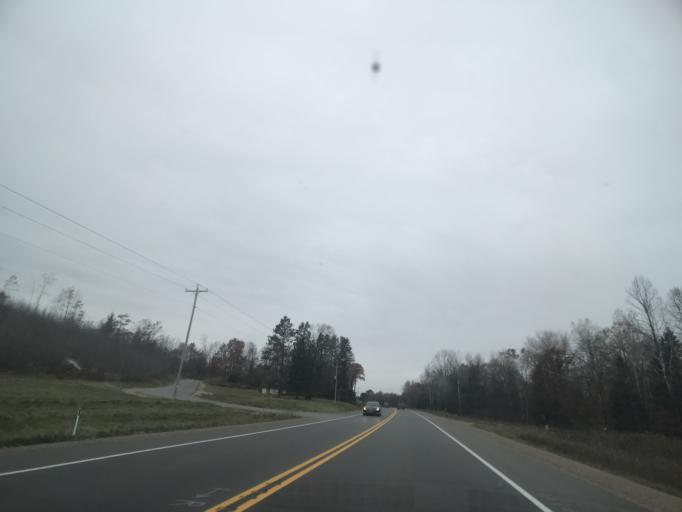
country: US
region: Wisconsin
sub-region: Menominee County
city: Legend Lake
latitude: 45.2927
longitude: -88.5118
